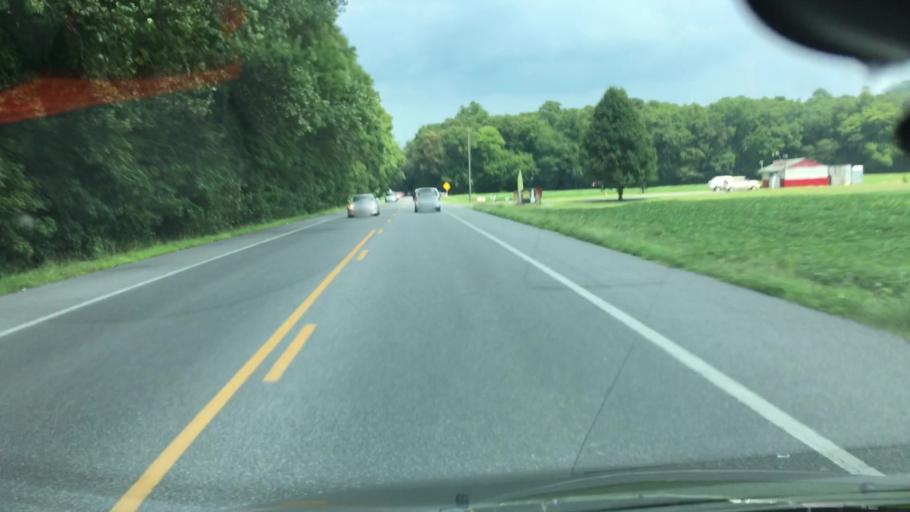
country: US
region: Maryland
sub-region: Worcester County
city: Ocean Pines
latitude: 38.3639
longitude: -75.1673
